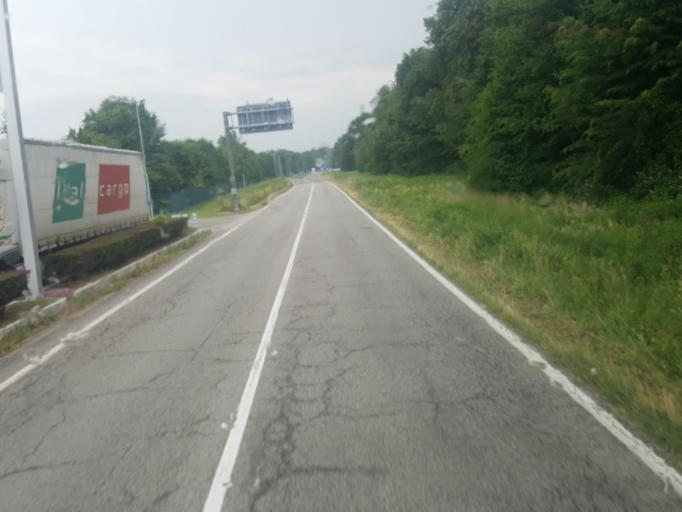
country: IT
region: Piedmont
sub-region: Provincia di Torino
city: Candiolo
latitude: 44.9663
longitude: 7.5705
